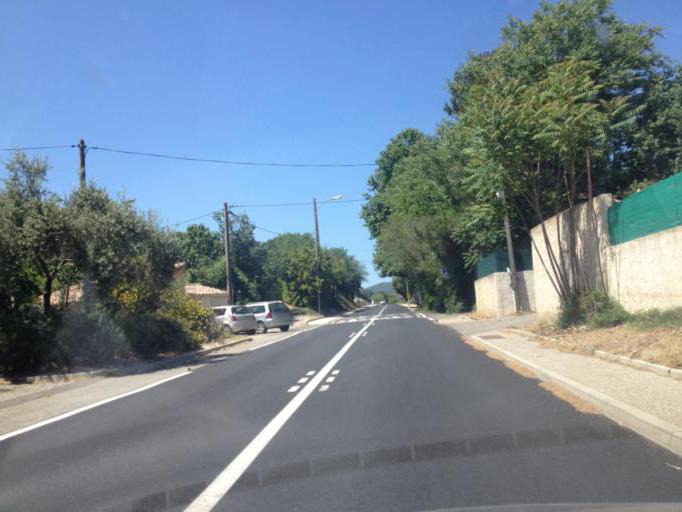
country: FR
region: Provence-Alpes-Cote d'Azur
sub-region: Departement du Vaucluse
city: Cadenet
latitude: 43.7377
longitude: 5.3661
